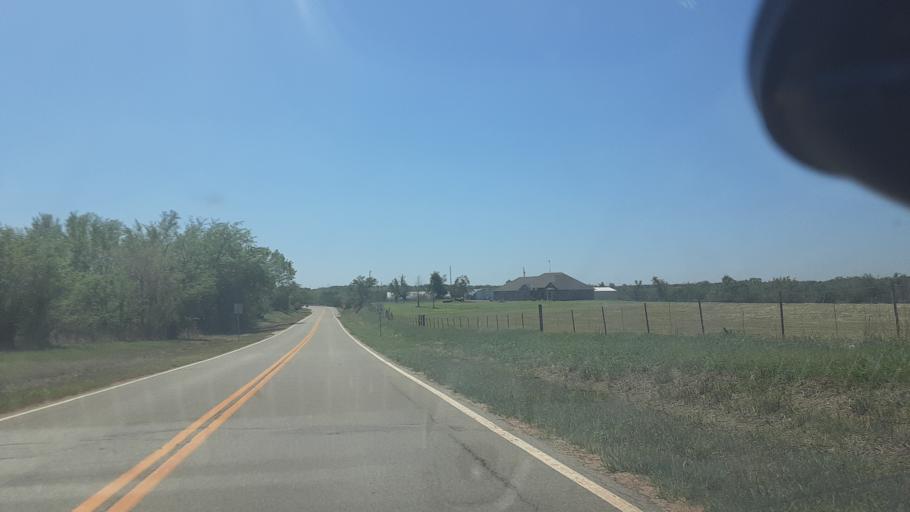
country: US
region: Oklahoma
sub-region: Logan County
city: Guthrie
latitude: 36.0566
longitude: -97.4078
